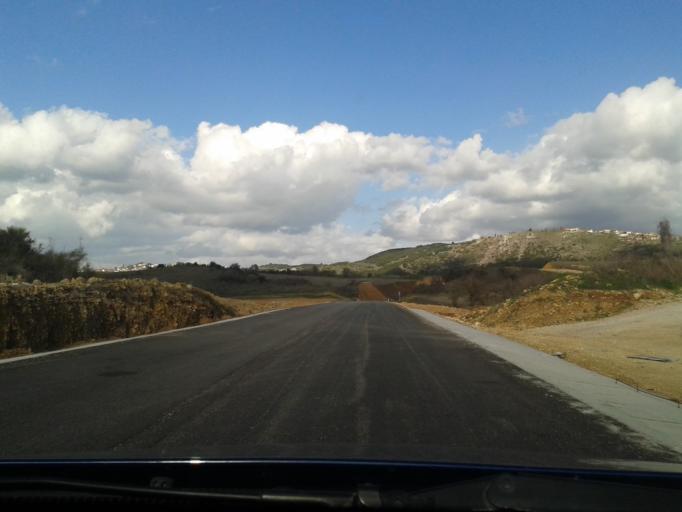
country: GR
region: West Greece
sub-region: Nomos Aitolias kai Akarnanias
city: Fitiai
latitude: 38.6839
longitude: 21.1682
